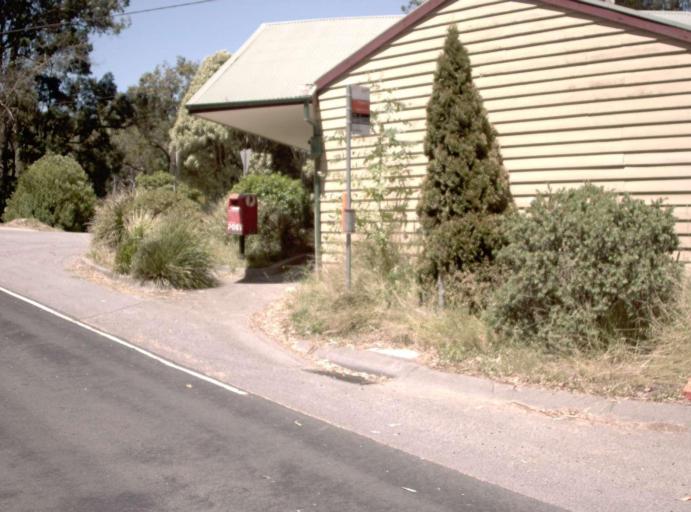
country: AU
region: Victoria
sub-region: Yarra Ranges
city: Ferny Creek
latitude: -37.8864
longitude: 145.3279
